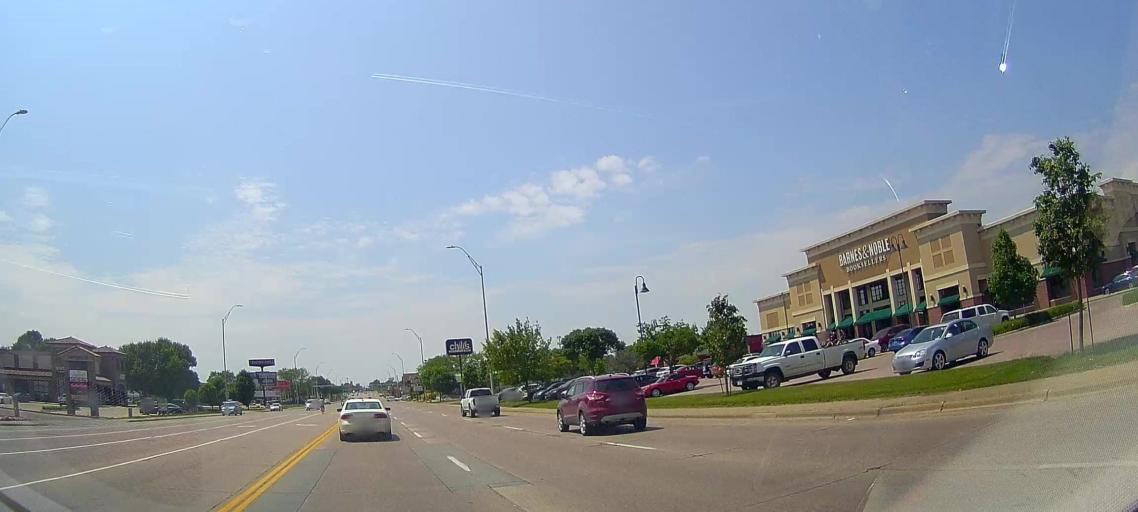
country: US
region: South Dakota
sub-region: Minnehaha County
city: Sioux Falls
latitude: 43.5150
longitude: -96.7715
